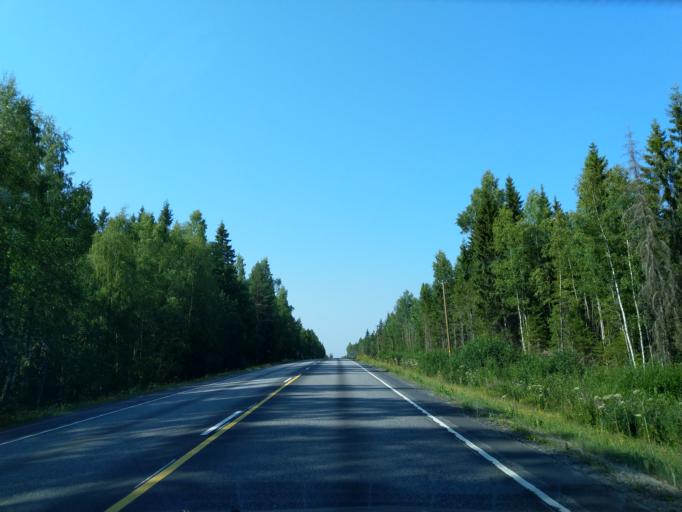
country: FI
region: Satakunta
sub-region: Pori
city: Pomarkku
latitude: 61.7244
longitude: 22.0605
